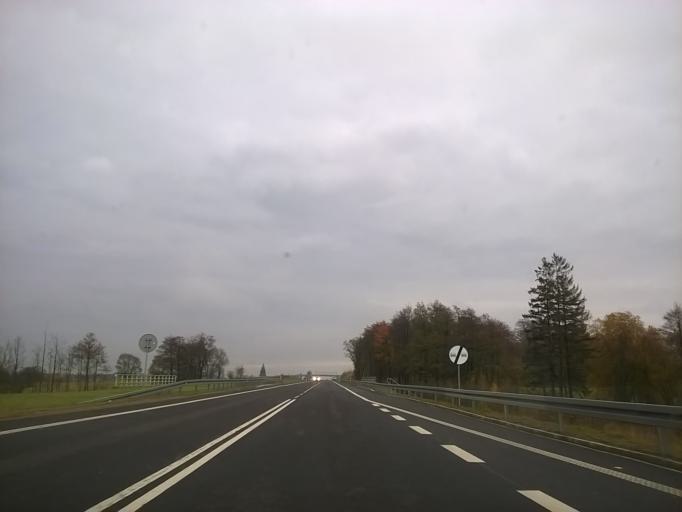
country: PL
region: Warmian-Masurian Voivodeship
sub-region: Powiat elblaski
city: Gronowo Gorne
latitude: 54.1833
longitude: 19.5532
